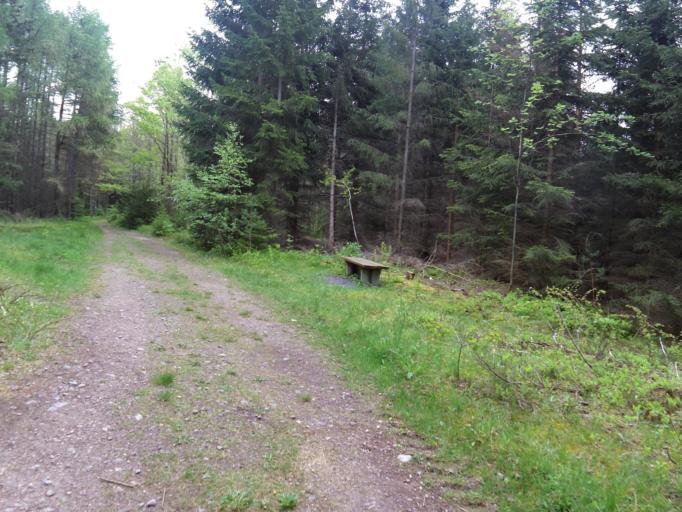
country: DE
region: Thuringia
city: Georgenthal
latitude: 50.8148
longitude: 10.6693
